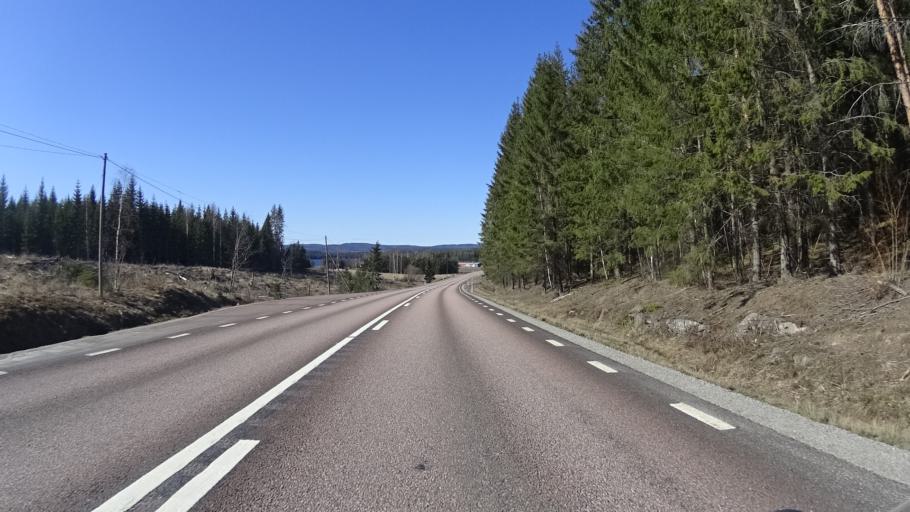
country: SE
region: Vaermland
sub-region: Sunne Kommun
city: Sunne
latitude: 59.6295
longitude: 12.9517
